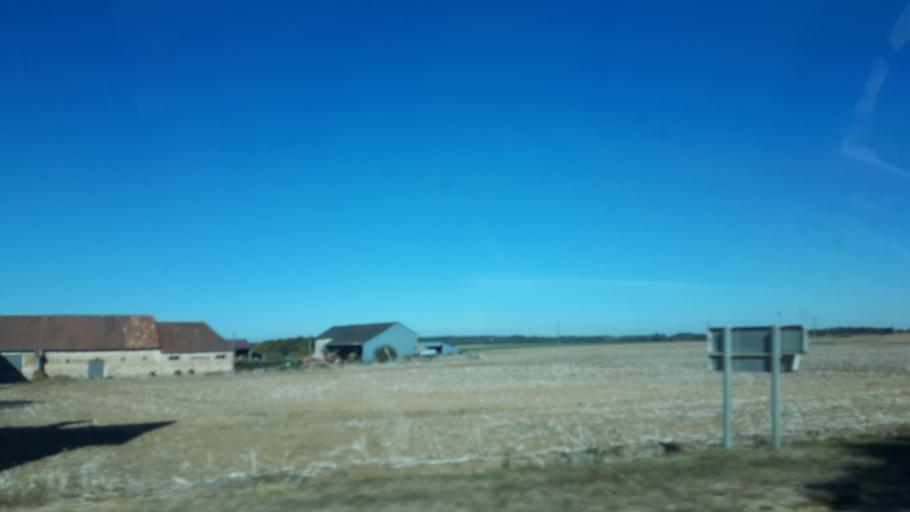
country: FR
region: Centre
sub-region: Departement d'Eure-et-Loir
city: La Chapelle-du-Noyer
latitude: 48.0530
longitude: 1.3229
